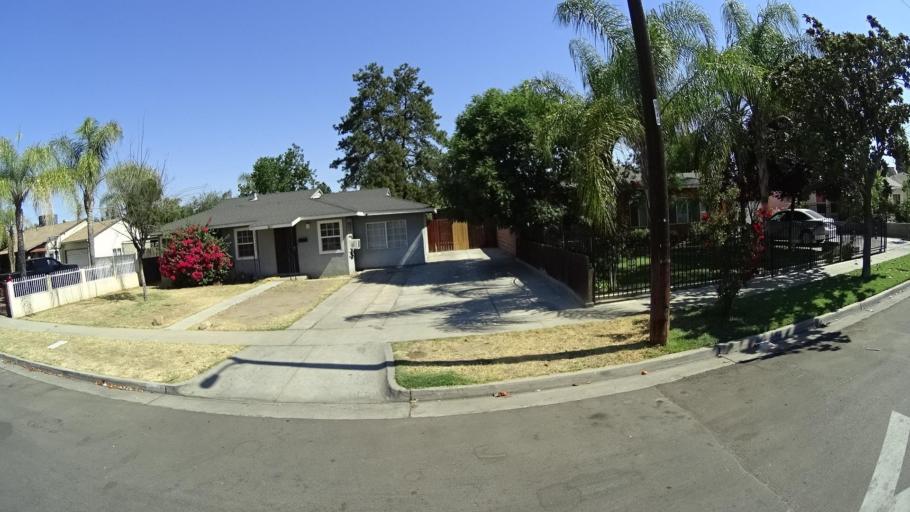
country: US
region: California
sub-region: Fresno County
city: Fresno
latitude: 36.7241
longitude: -119.7606
